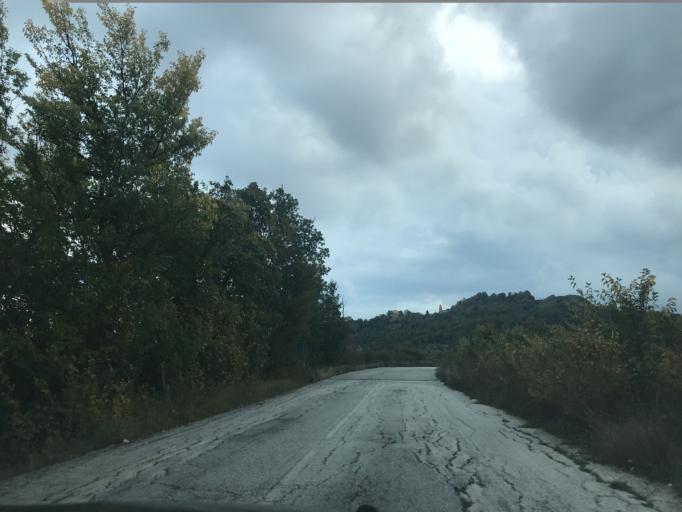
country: IT
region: Molise
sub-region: Provincia di Campobasso
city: Duronia
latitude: 41.6700
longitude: 14.4611
